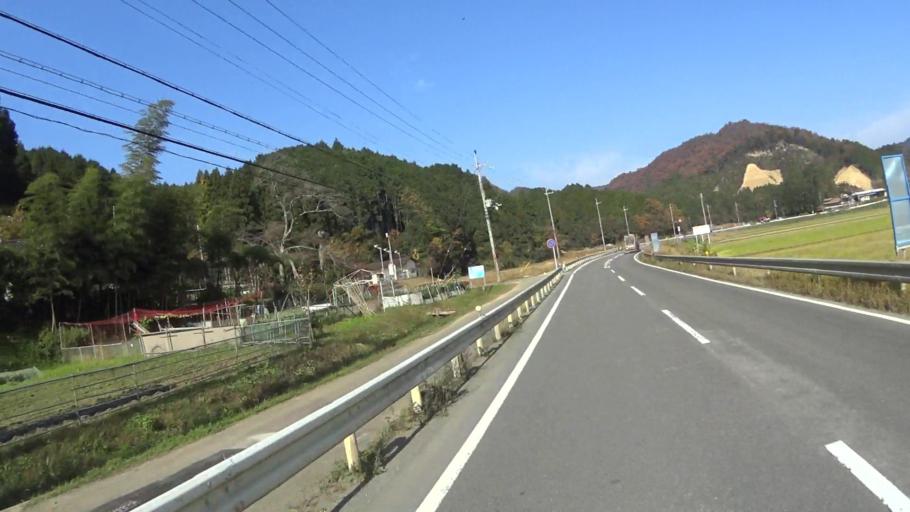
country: JP
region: Kyoto
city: Fukuchiyama
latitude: 35.4030
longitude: 135.1825
